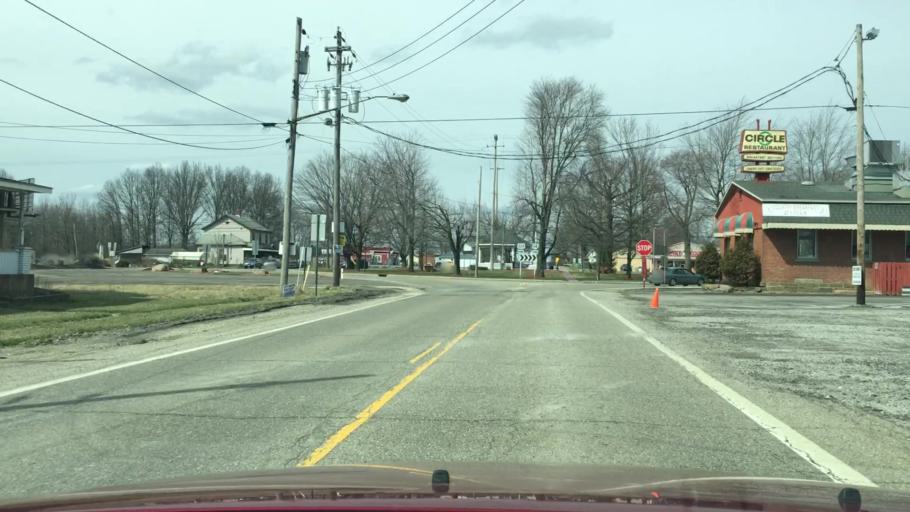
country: US
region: Ohio
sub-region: Mahoning County
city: Sebring
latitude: 41.0237
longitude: -81.0504
